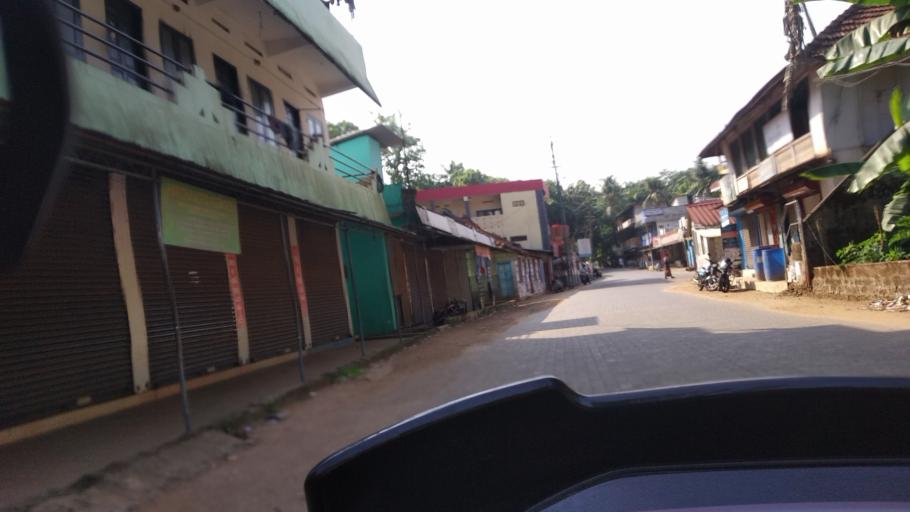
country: IN
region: Kerala
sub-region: Ernakulam
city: Piravam
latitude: 9.8665
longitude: 76.5075
